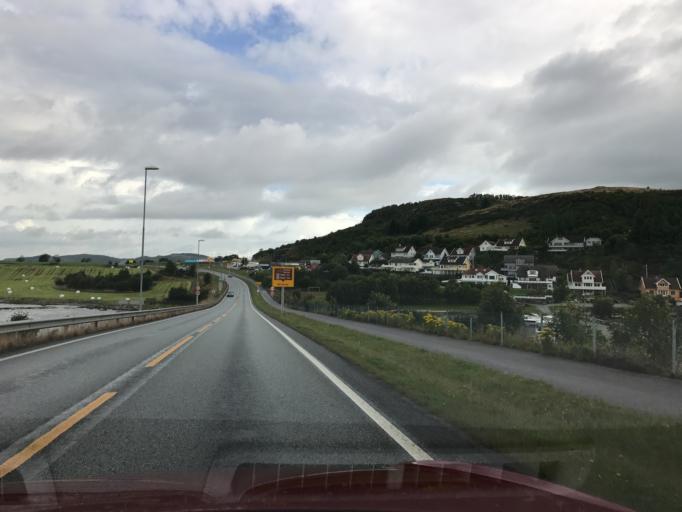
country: NO
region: Rogaland
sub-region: Rennesoy
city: Vikevag
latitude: 59.0606
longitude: 5.6772
